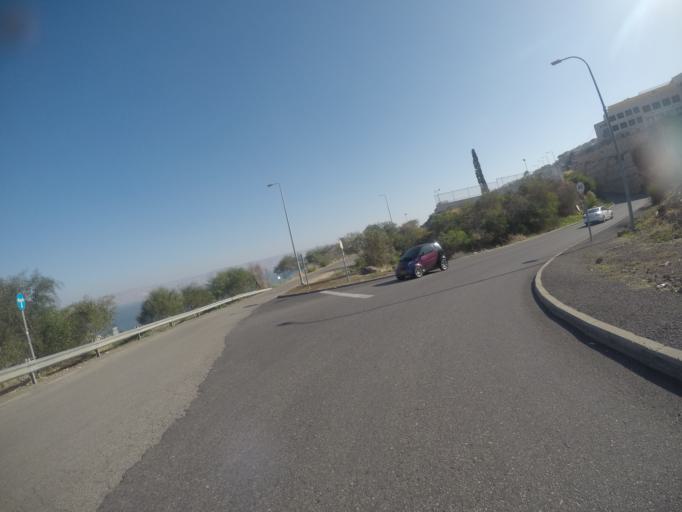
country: IL
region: Northern District
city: Tiberias
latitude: 32.7895
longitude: 35.5282
